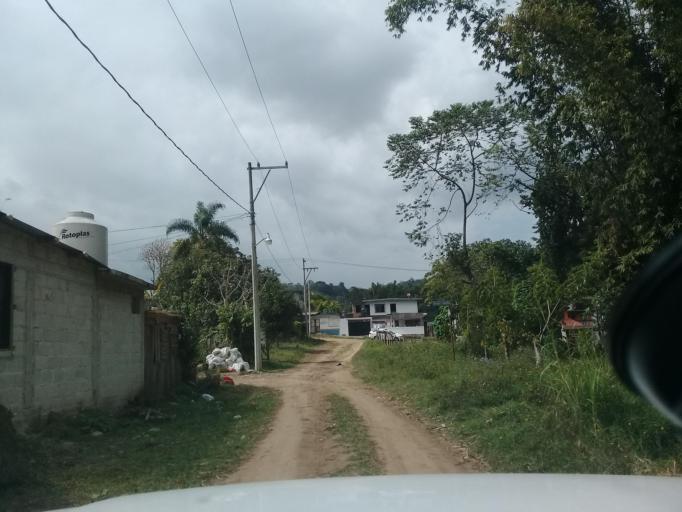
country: MX
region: Veracruz
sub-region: Xalapa
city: Fraccionamiento las Fuentes
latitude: 19.4742
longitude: -96.8769
